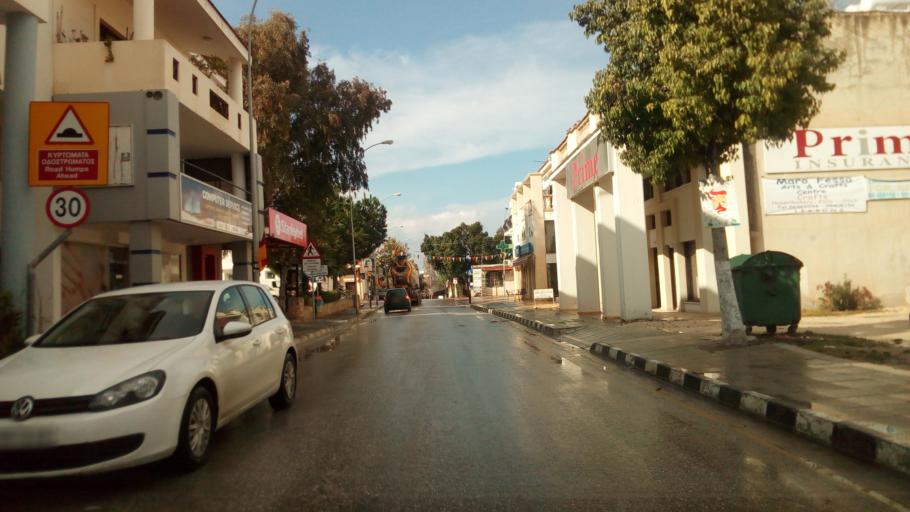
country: CY
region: Pafos
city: Polis
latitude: 35.0344
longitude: 32.4252
